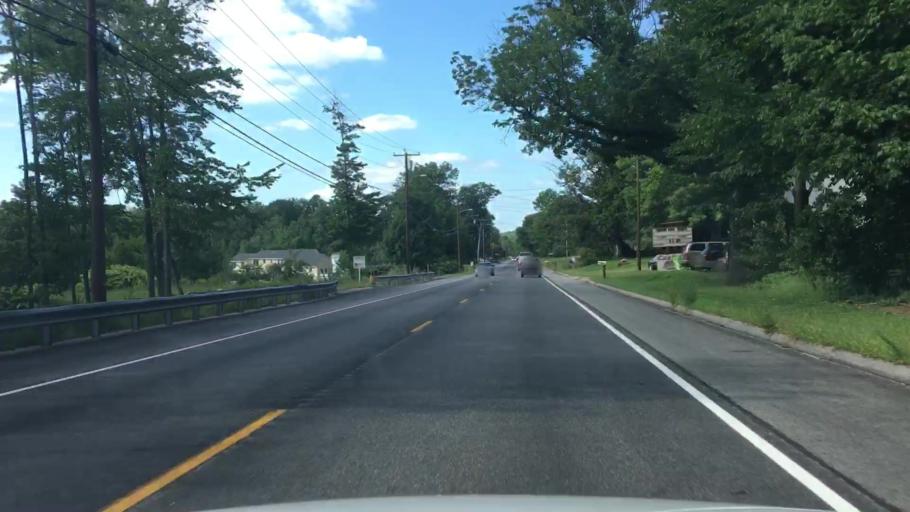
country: US
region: Maine
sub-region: Cumberland County
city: South Windham
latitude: 43.7702
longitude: -70.3786
